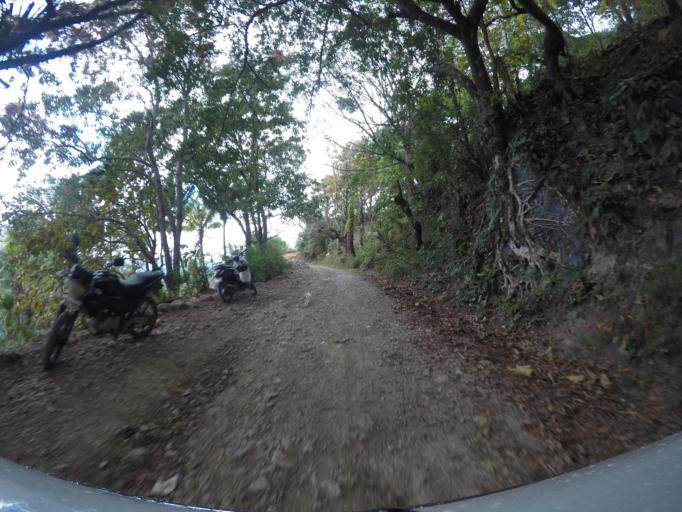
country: TL
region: Baucau
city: Baucau
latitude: -8.6419
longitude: 126.6381
